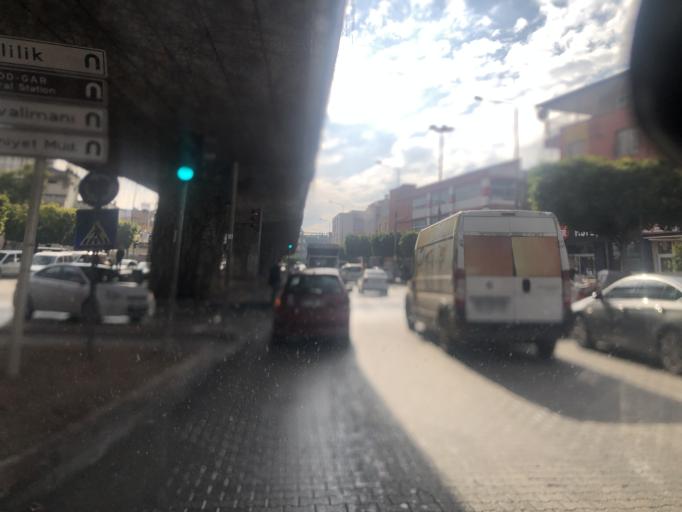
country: TR
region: Adana
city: Seyhan
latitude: 36.9827
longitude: 35.3205
